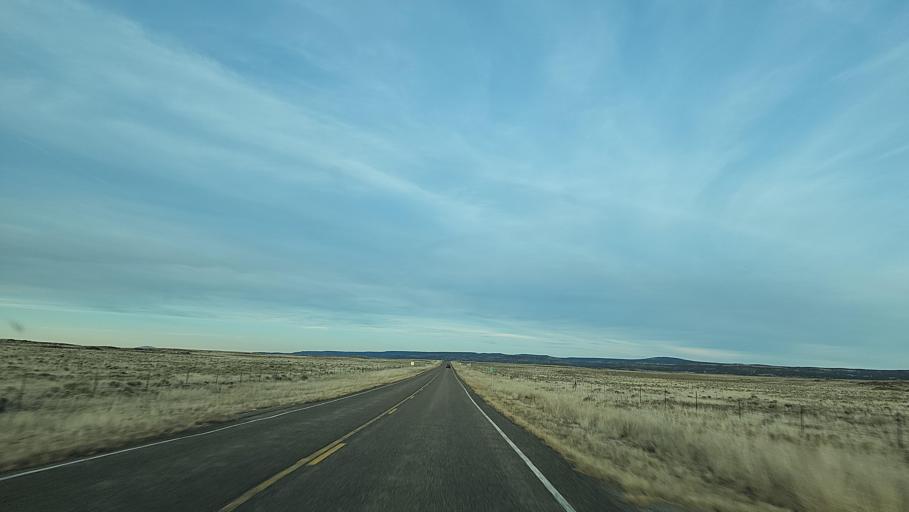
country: US
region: New Mexico
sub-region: Cibola County
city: Grants
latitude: 34.6847
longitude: -108.0691
